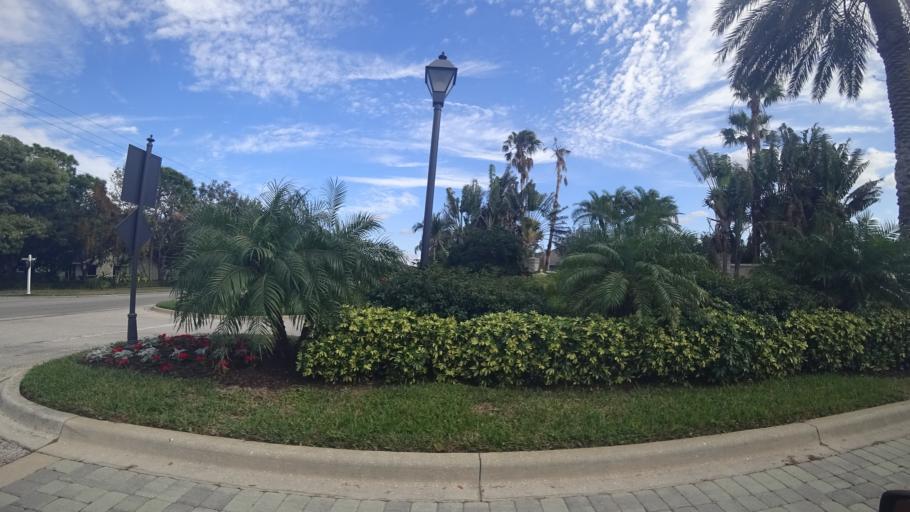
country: US
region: Florida
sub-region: Manatee County
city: West Bradenton
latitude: 27.5179
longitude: -82.6492
